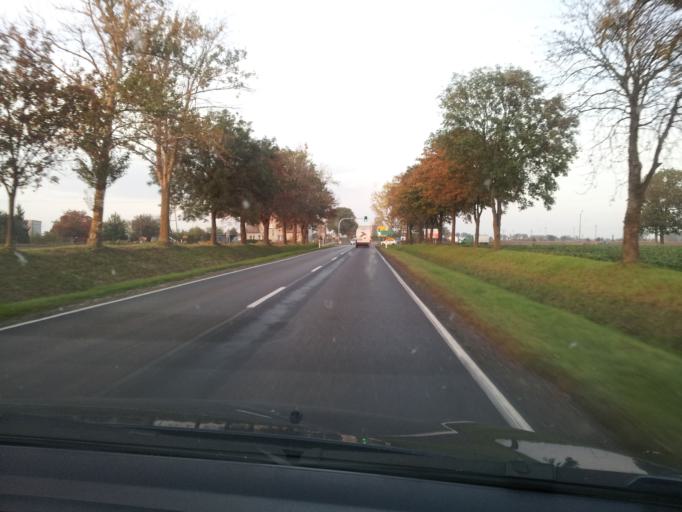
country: PL
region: Kujawsko-Pomorskie
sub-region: Powiat inowroclawski
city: Wierzchoslawice
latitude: 52.8668
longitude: 18.3641
